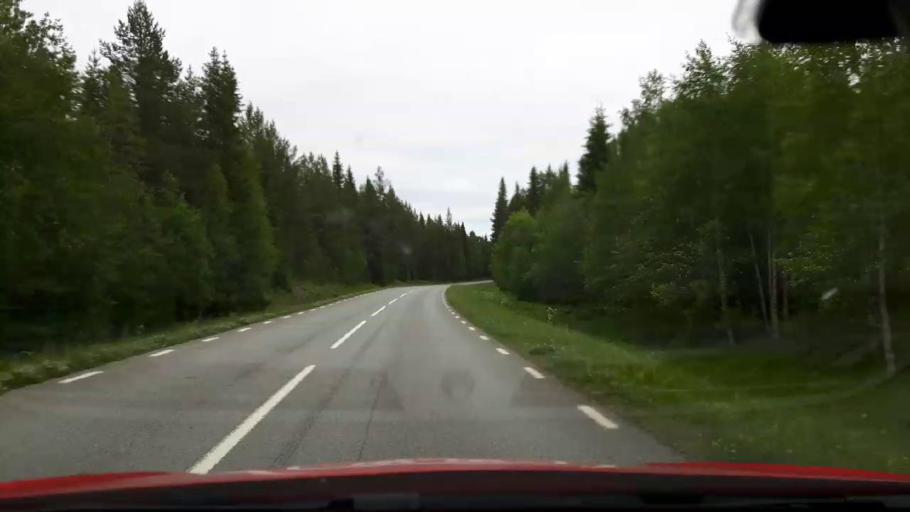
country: SE
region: Jaemtland
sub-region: Stroemsunds Kommun
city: Stroemsund
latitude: 63.4521
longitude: 15.4664
